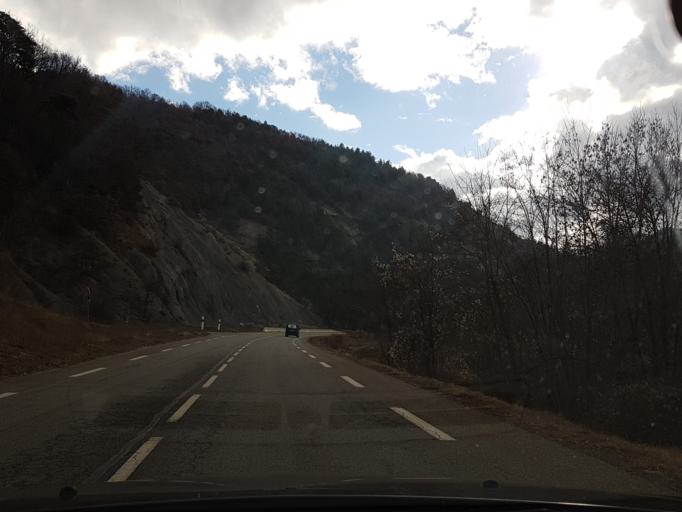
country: FR
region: Provence-Alpes-Cote d'Azur
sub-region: Departement des Hautes-Alpes
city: Gap
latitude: 44.5182
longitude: 6.0634
